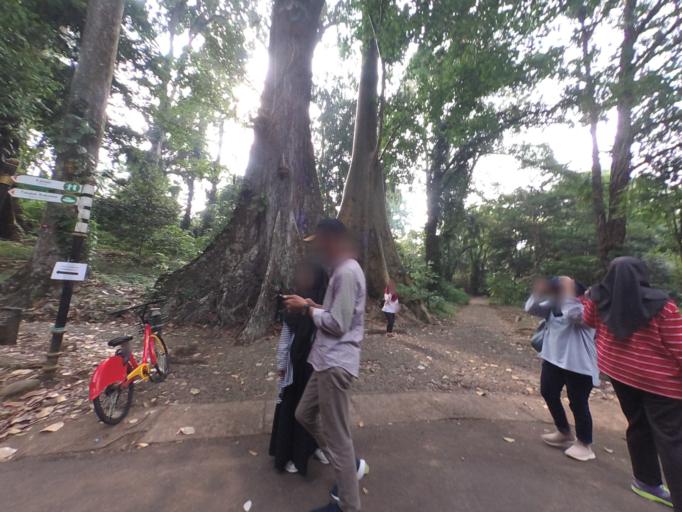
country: ID
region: West Java
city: Bogor
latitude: -6.5950
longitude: 106.7998
